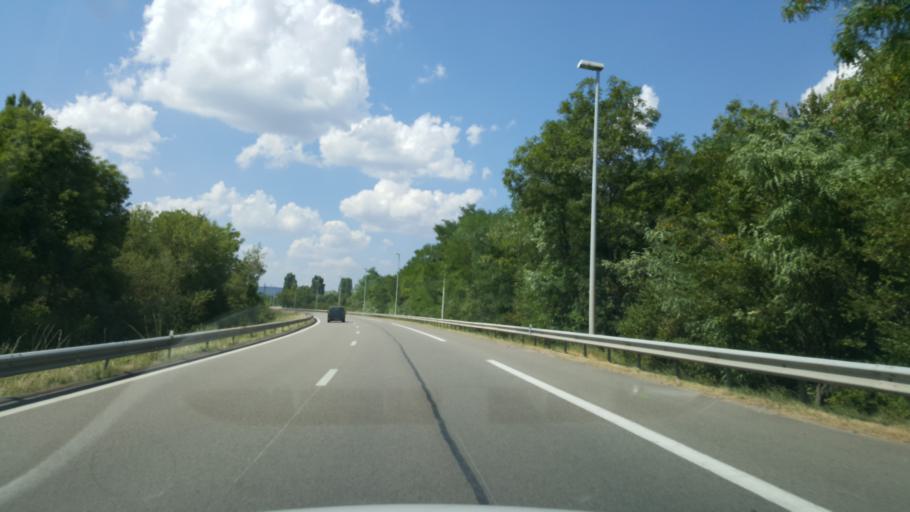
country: FR
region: Bourgogne
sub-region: Departement de la Cote-d'Or
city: Beaune
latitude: 47.0308
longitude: 4.8732
